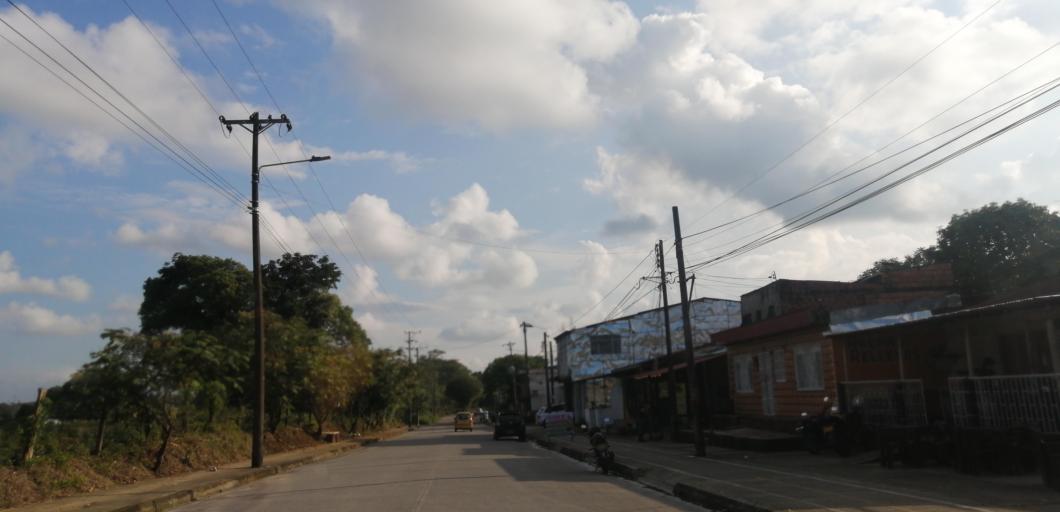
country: CO
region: Meta
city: Acacias
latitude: 3.9800
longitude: -73.7652
